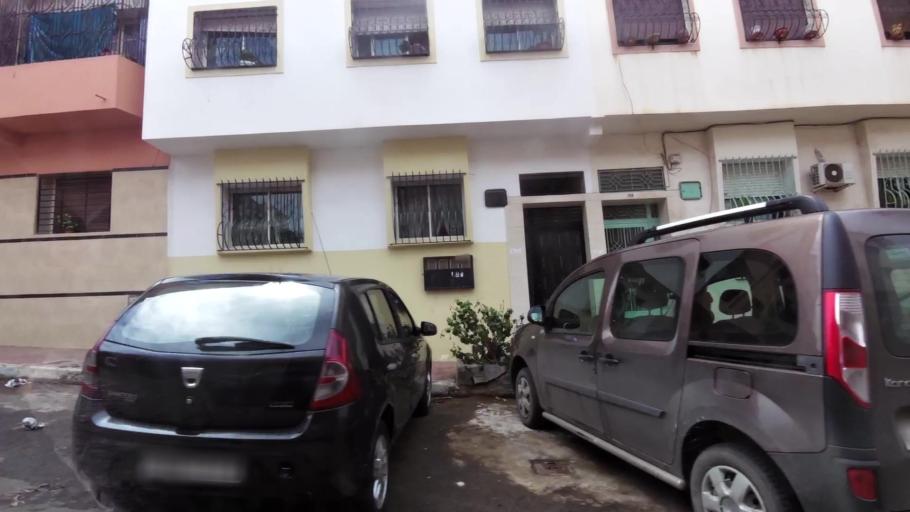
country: MA
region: Grand Casablanca
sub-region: Casablanca
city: Casablanca
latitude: 33.5408
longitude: -7.6778
